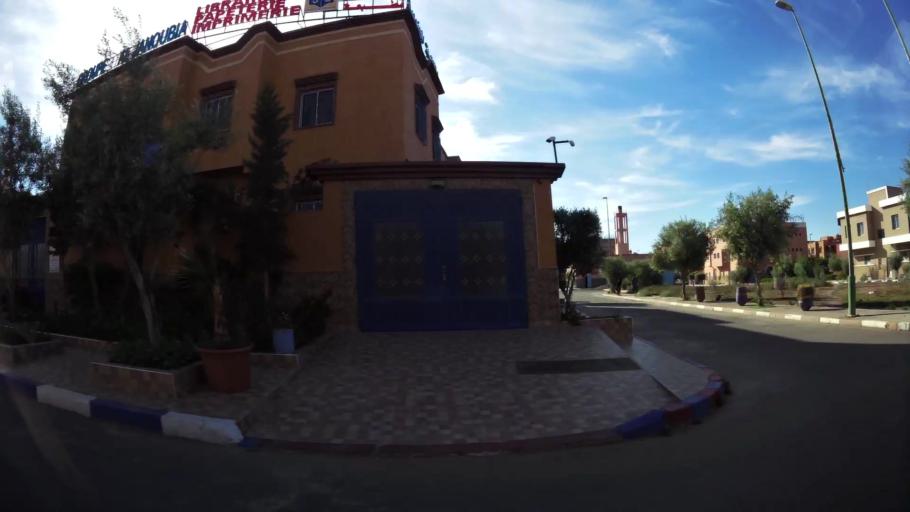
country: MA
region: Marrakech-Tensift-Al Haouz
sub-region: Marrakech
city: Marrakesh
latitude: 31.6839
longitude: -8.0649
